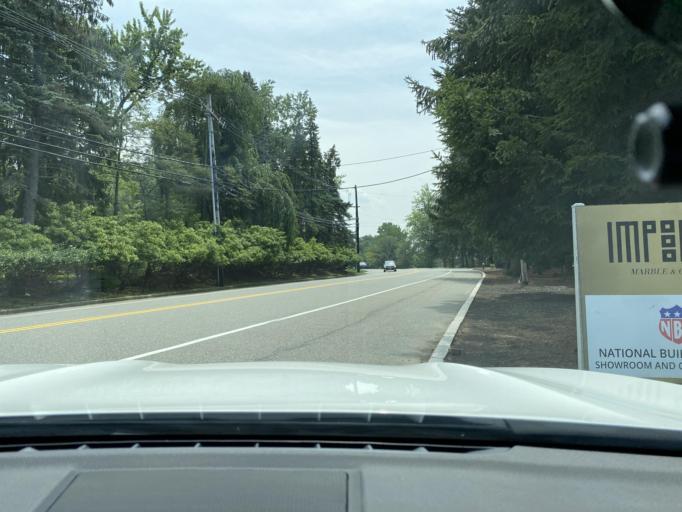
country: US
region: New Jersey
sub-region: Bergen County
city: Ramsey
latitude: 41.0694
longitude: -74.1204
